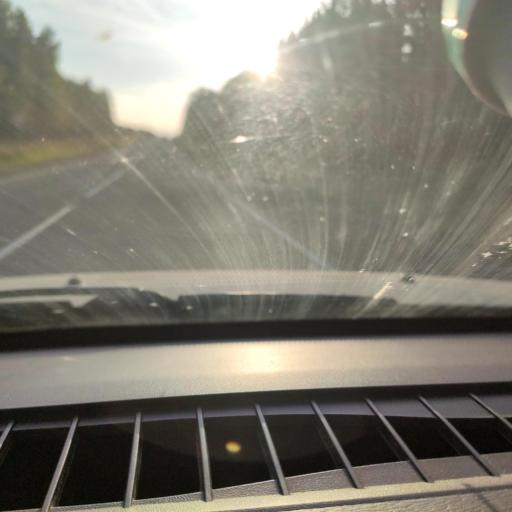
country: RU
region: Kirov
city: Belaya Kholunitsa
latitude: 58.8141
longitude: 50.5862
